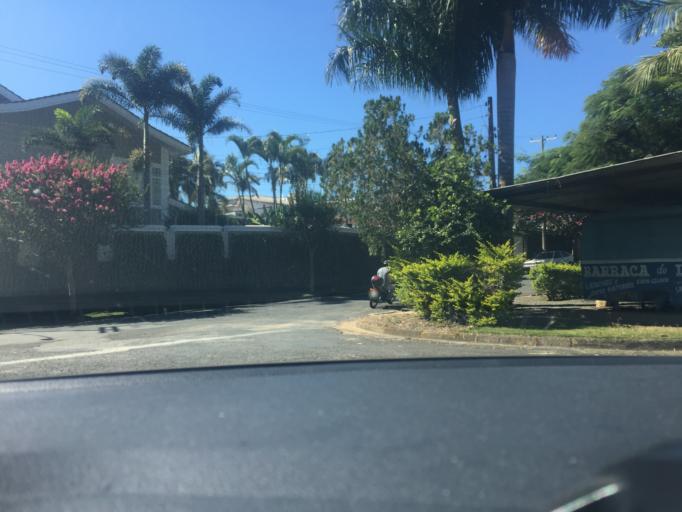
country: BR
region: Sao Paulo
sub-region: Santo Antonio Do Jardim
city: Espirito Santo do Pinhal
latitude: -22.1805
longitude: -46.7444
